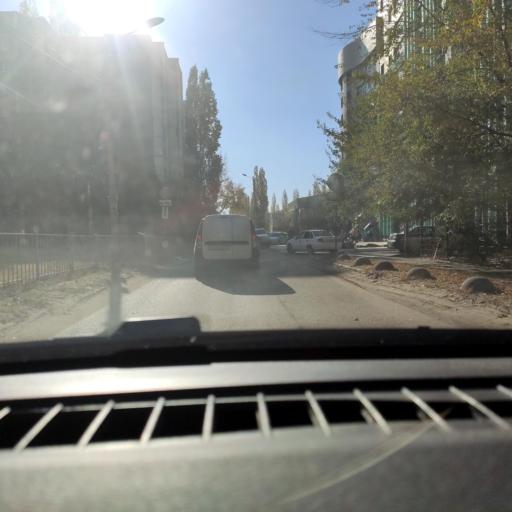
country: RU
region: Voronezj
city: Podgornoye
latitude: 51.7185
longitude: 39.1669
